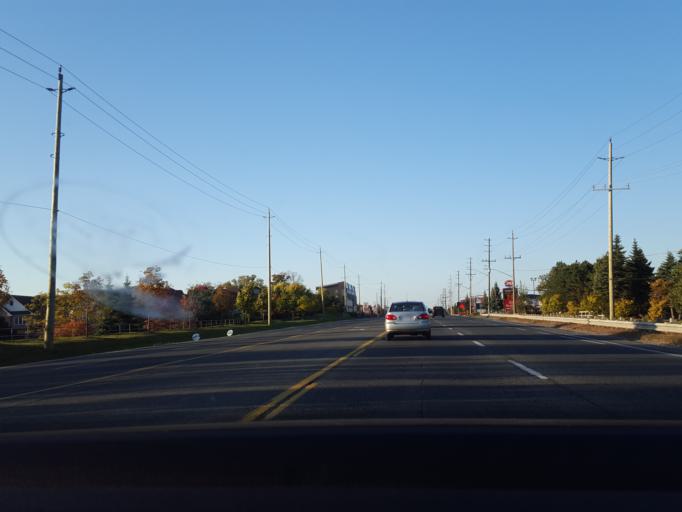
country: CA
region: Ontario
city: Newmarket
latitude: 44.0296
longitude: -79.4745
